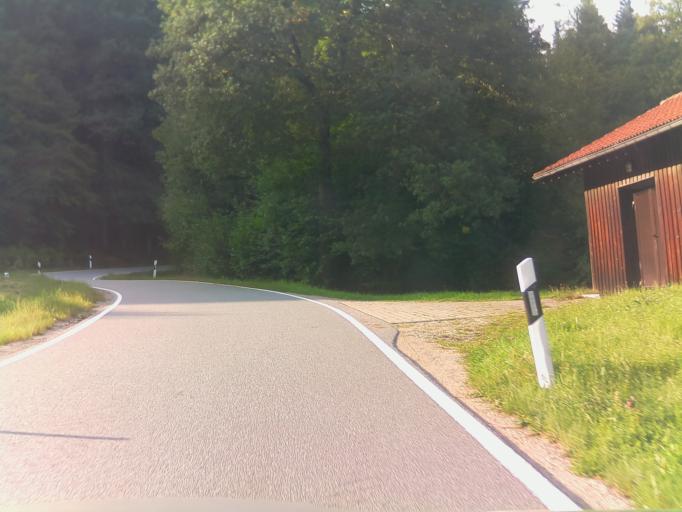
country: DE
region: Hesse
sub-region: Regierungsbezirk Darmstadt
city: Rothenberg
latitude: 49.5557
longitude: 8.8965
